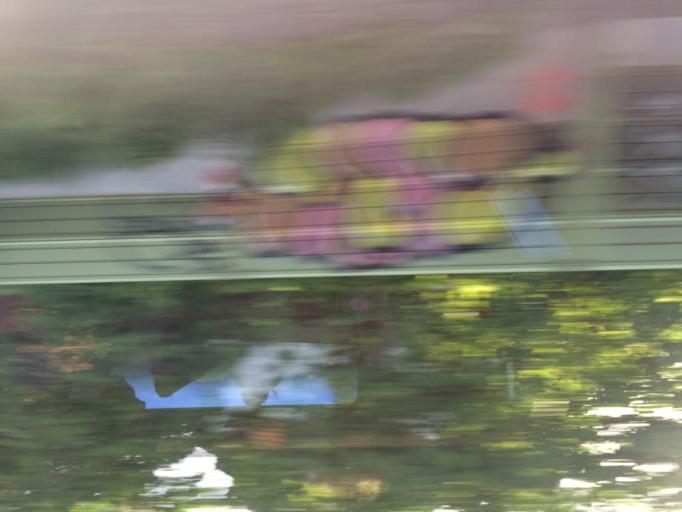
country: DE
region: Hesse
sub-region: Regierungsbezirk Darmstadt
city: Kiedrich
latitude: 50.0206
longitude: 8.0911
